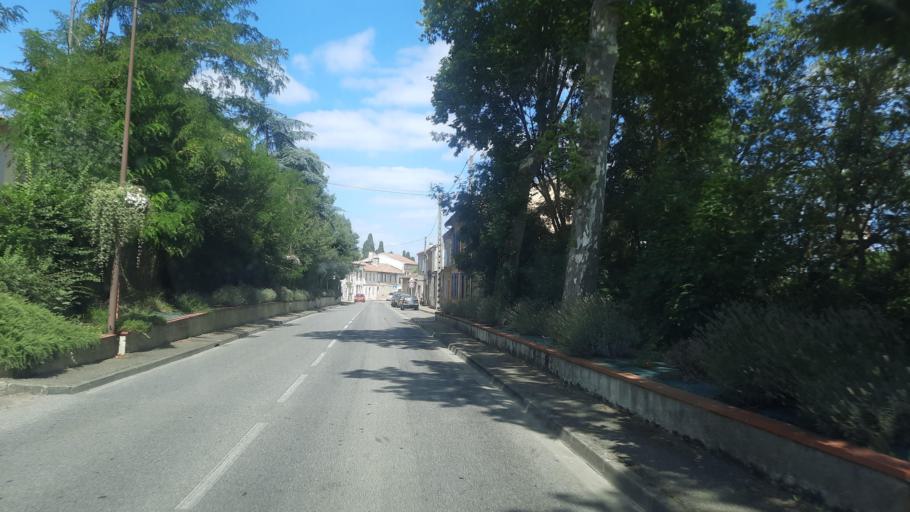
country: FR
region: Midi-Pyrenees
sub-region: Departement du Gers
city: Lombez
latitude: 43.4738
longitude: 0.9070
